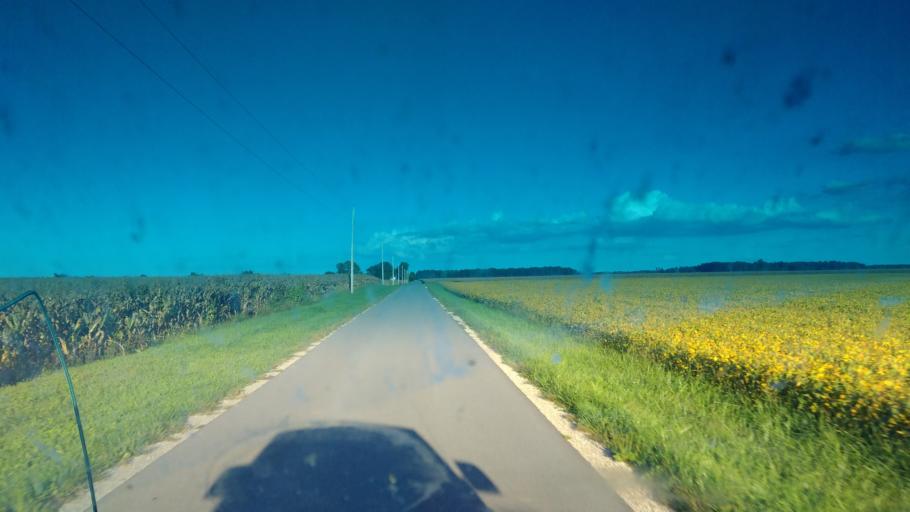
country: US
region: Ohio
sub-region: Wyandot County
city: Upper Sandusky
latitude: 40.8909
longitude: -83.2740
